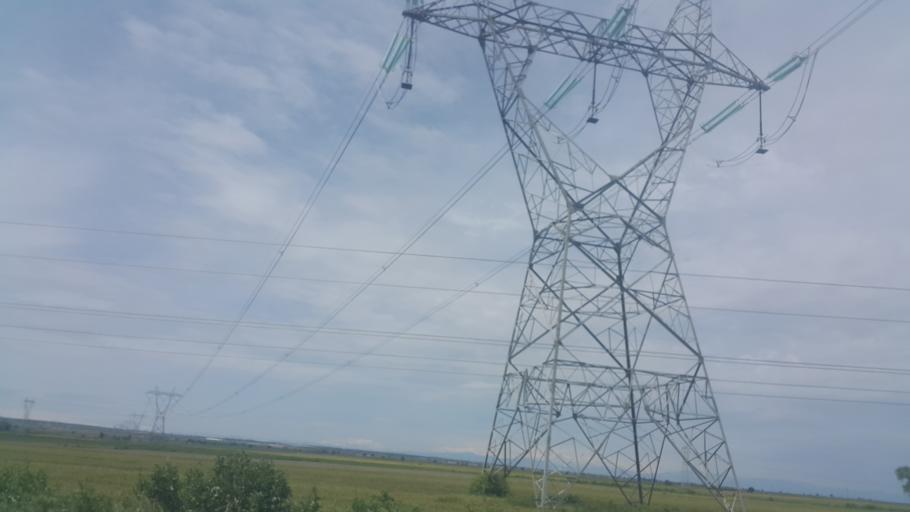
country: TR
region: Adana
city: Yakapinar
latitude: 37.0118
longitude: 35.7065
